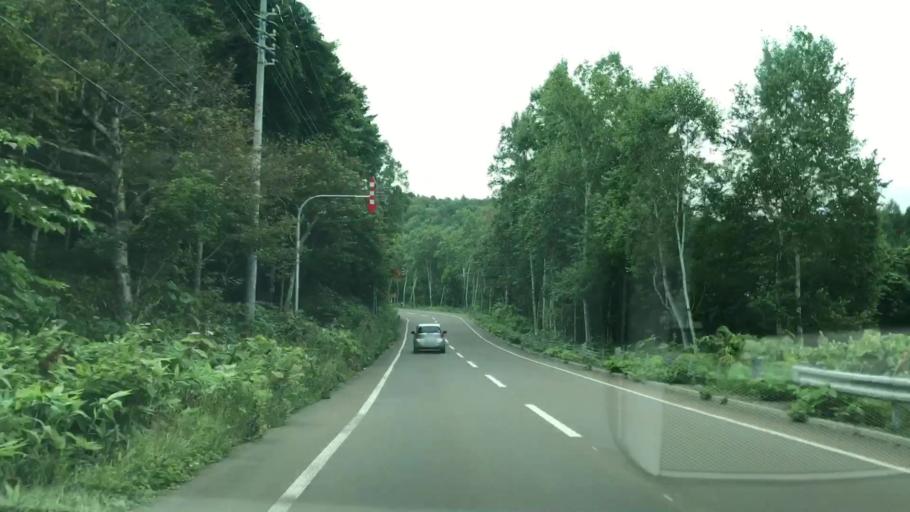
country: JP
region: Hokkaido
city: Yoichi
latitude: 43.1307
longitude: 140.8266
